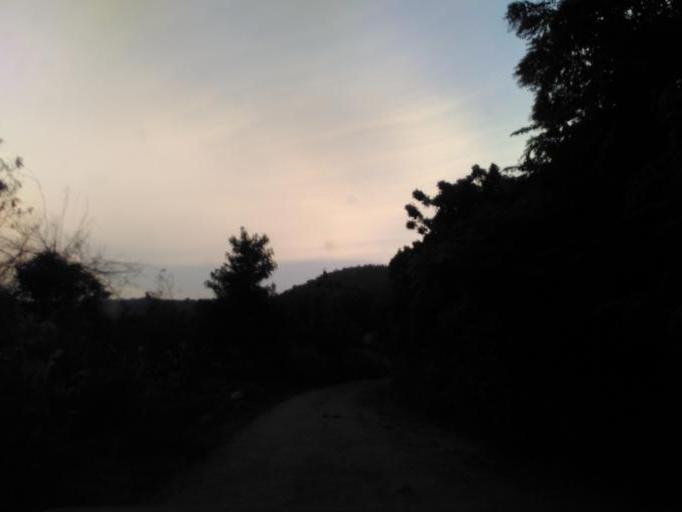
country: GH
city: Bekwai
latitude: 6.5123
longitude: -1.4434
